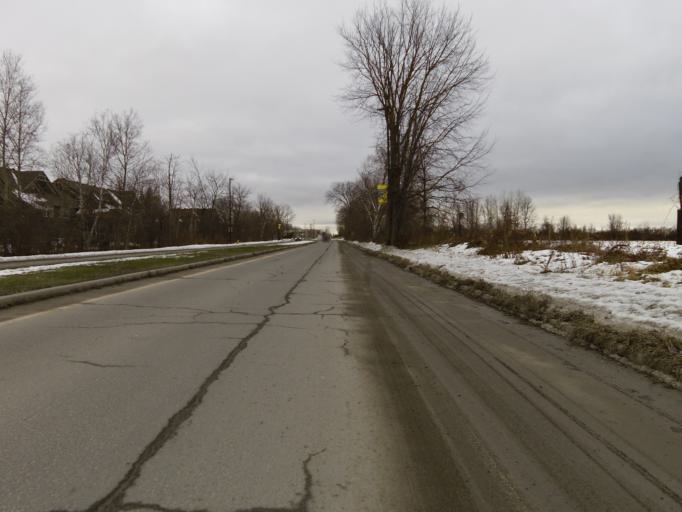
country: CA
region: Ontario
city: Bells Corners
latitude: 45.3447
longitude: -75.9005
